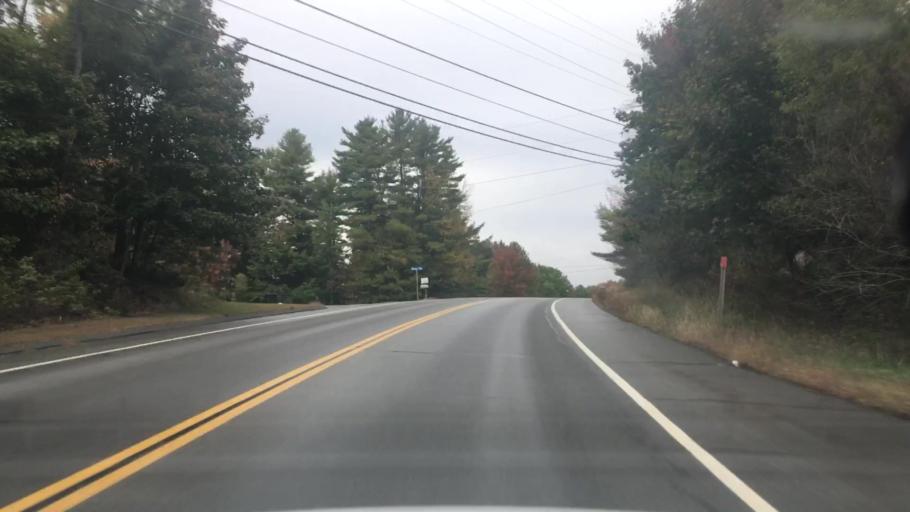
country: US
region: Maine
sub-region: Kennebec County
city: Augusta
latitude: 44.3806
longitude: -69.8016
